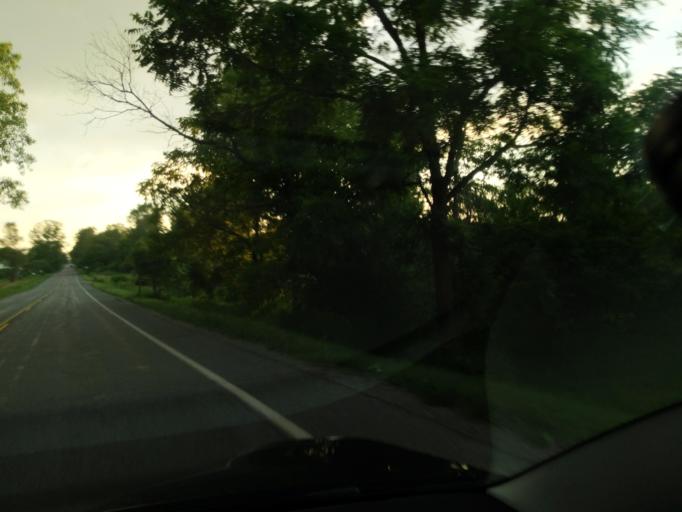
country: US
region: Michigan
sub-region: Ingham County
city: Mason
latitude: 42.5238
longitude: -84.3733
